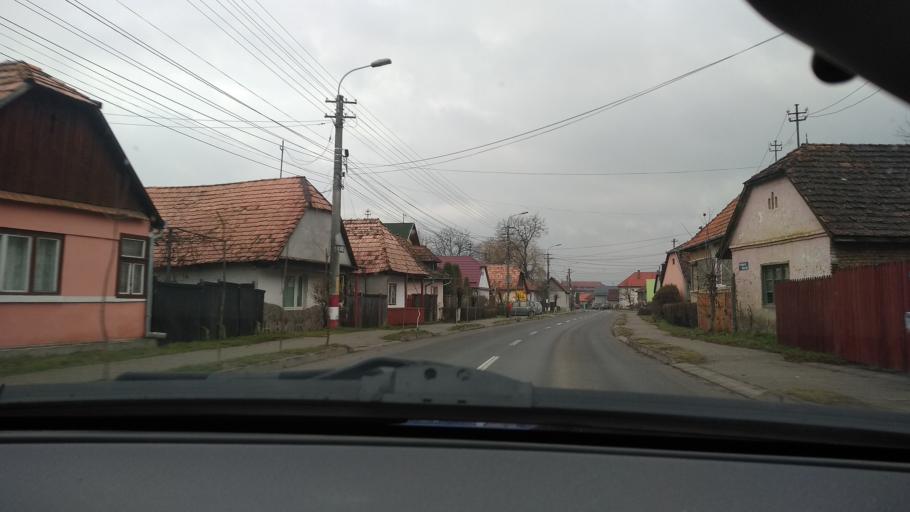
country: RO
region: Mures
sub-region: Oras Sovata
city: Sovata
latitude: 46.5844
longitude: 25.0603
